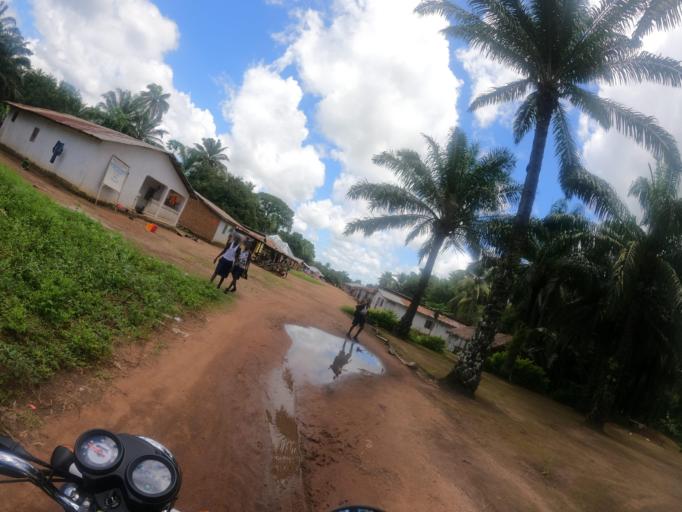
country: SL
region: Northern Province
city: Makeni
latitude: 8.8637
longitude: -12.0980
